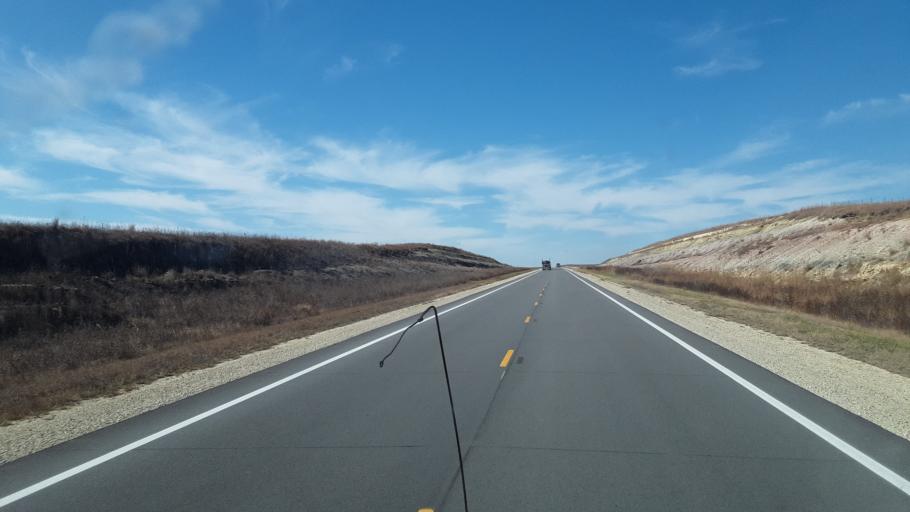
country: US
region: Kansas
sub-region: Chase County
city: Cottonwood Falls
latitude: 38.3627
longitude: -96.6891
